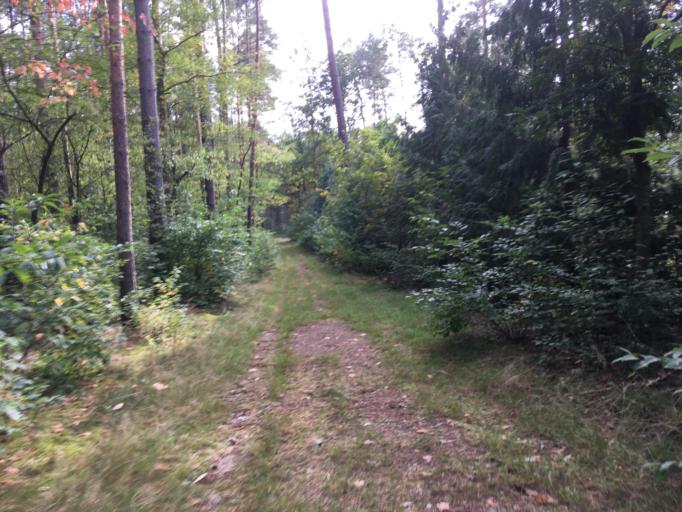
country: DE
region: Brandenburg
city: Birkenwerder
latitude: 52.7044
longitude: 13.3207
